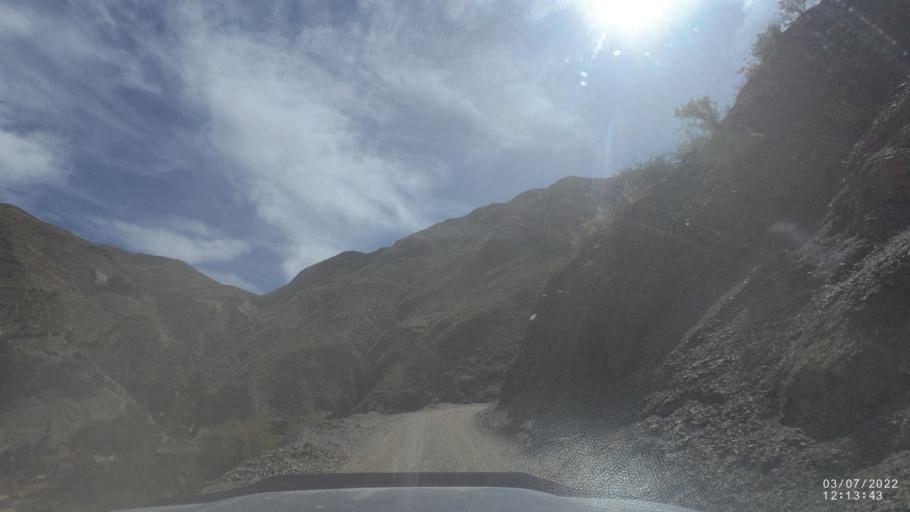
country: BO
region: Cochabamba
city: Irpa Irpa
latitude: -17.8339
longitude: -66.6123
